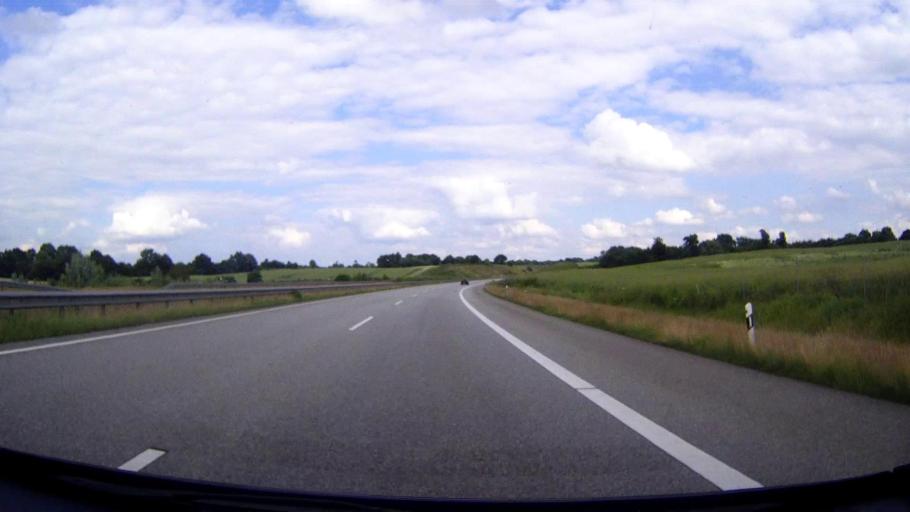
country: DE
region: Schleswig-Holstein
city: Strukdorf
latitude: 53.9253
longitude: 10.4754
